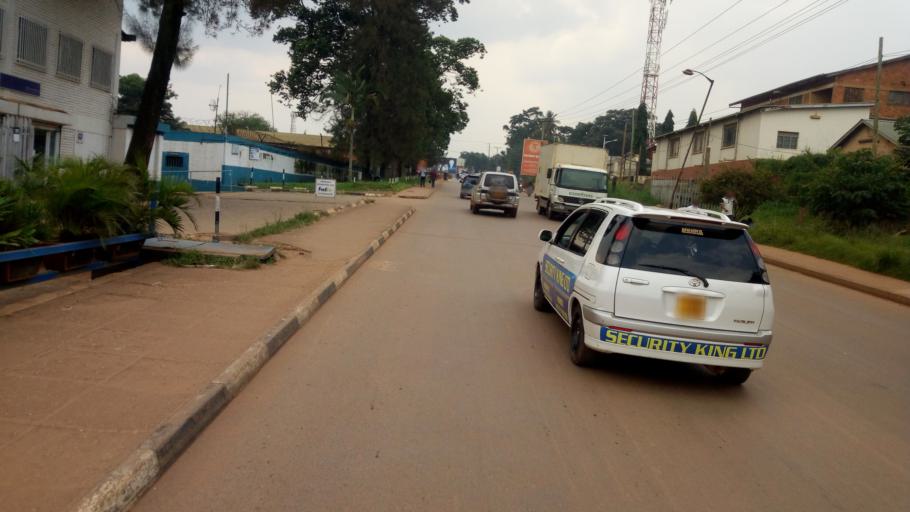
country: UG
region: Central Region
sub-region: Kampala District
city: Kampala
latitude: 0.3187
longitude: 32.6118
